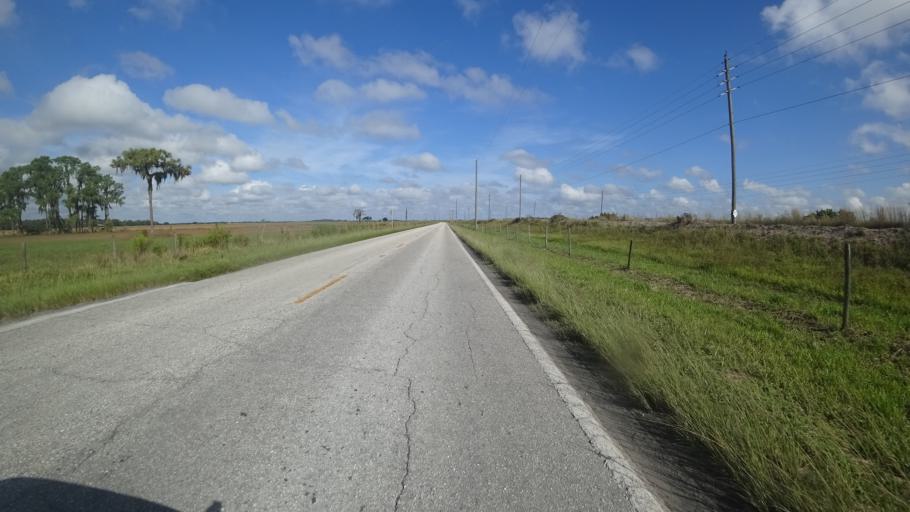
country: US
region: Florida
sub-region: Hardee County
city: Wauchula
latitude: 27.5154
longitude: -82.0726
